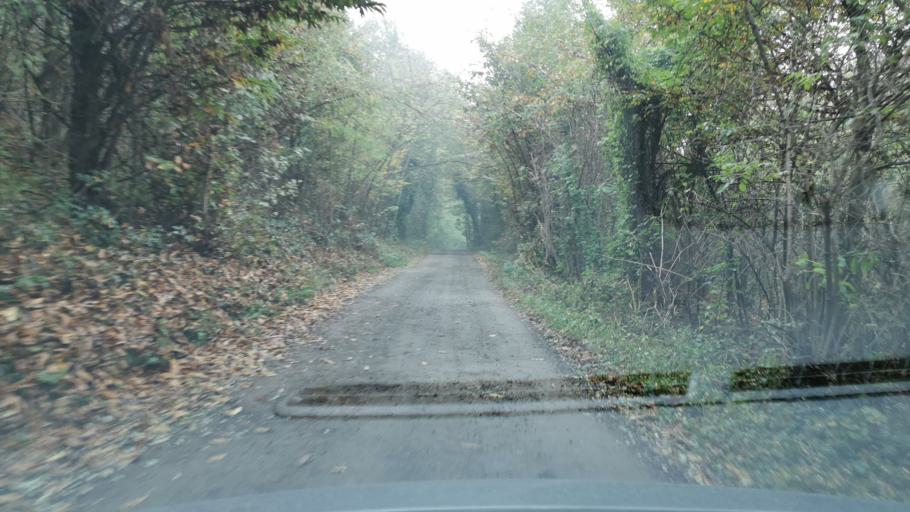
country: IT
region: Piedmont
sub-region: Provincia di Torino
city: Scarmagno
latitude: 45.3839
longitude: 7.8343
